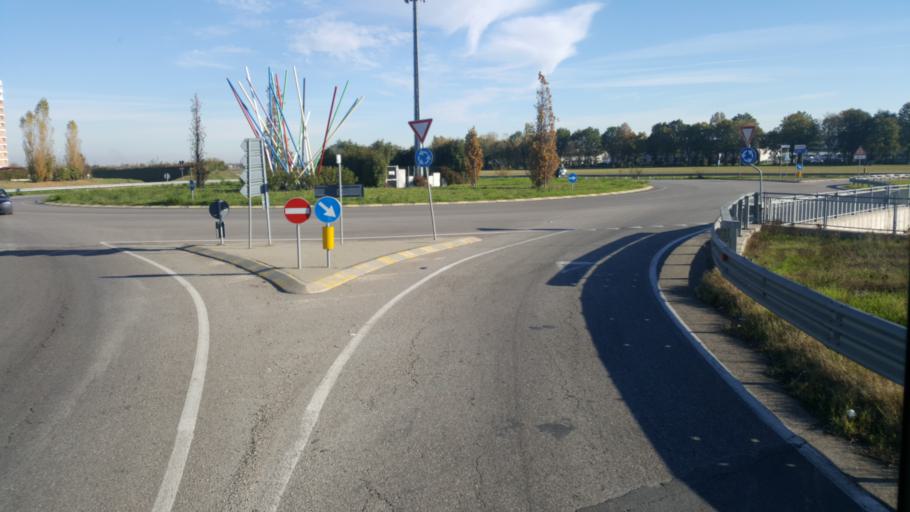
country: IT
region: Emilia-Romagna
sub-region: Provincia di Bologna
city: Calderara di Reno
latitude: 44.5564
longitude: 11.2760
